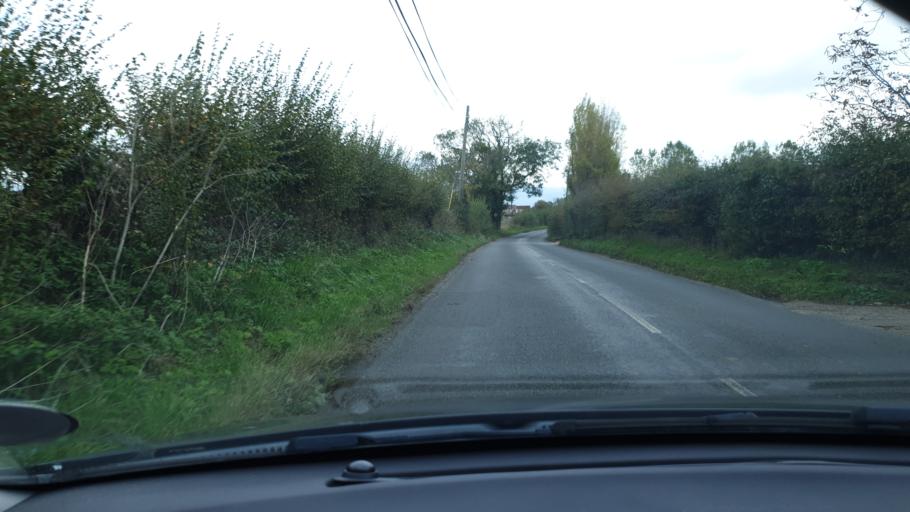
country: GB
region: England
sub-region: Essex
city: Mistley
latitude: 51.9375
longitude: 1.0949
